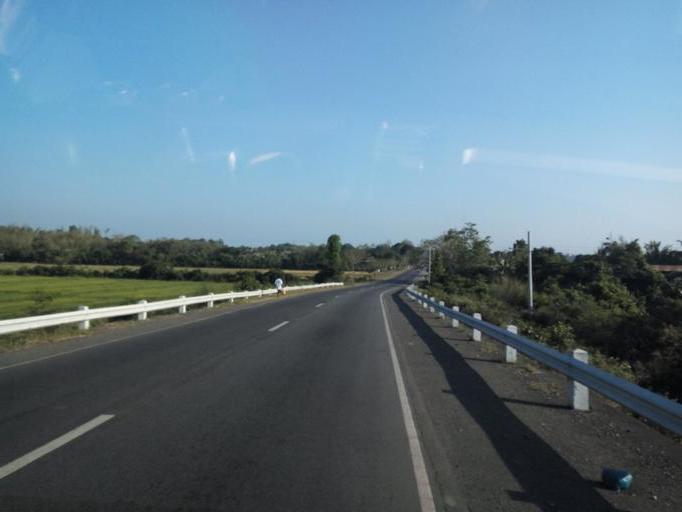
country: PH
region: Cagayan Valley
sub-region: Province of Cagayan
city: Iguig
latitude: 17.7311
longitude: 121.7387
